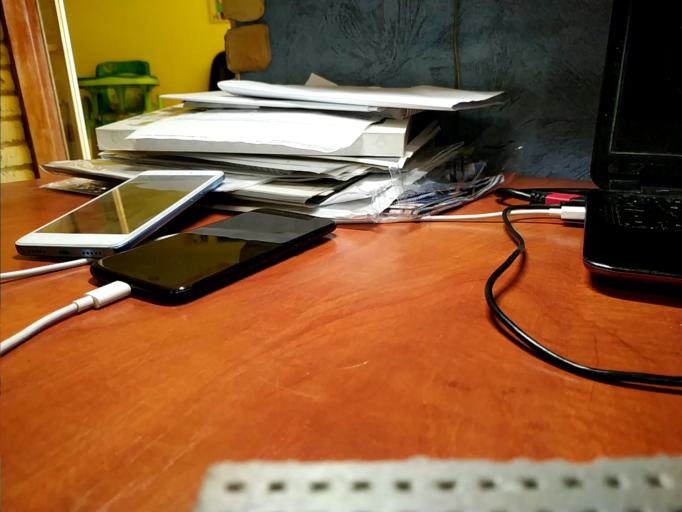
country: RU
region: Tverskaya
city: Kalashnikovo
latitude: 57.3991
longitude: 35.2388
